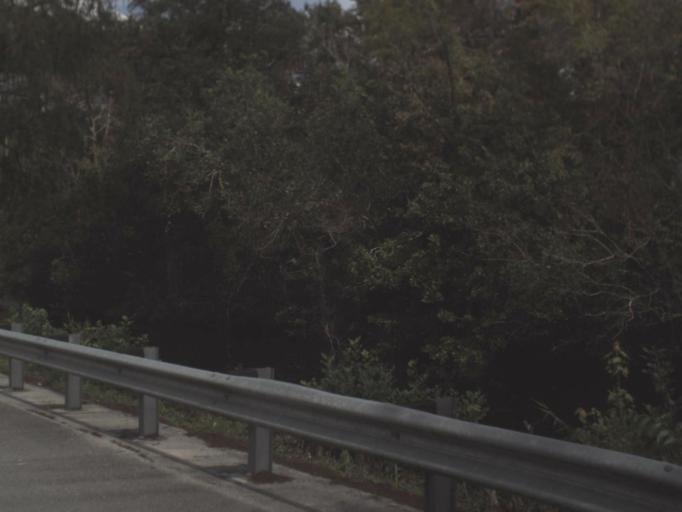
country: US
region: Florida
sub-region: Collier County
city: Lely Resort
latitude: 25.9372
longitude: -81.3572
